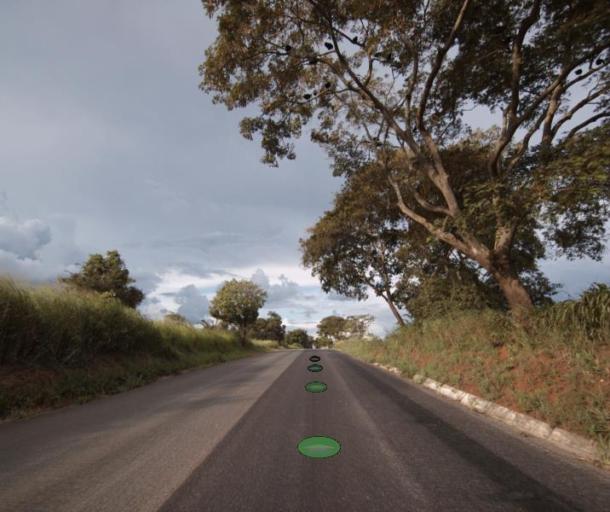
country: BR
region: Goias
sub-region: Itapaci
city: Itapaci
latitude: -15.1244
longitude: -49.5053
